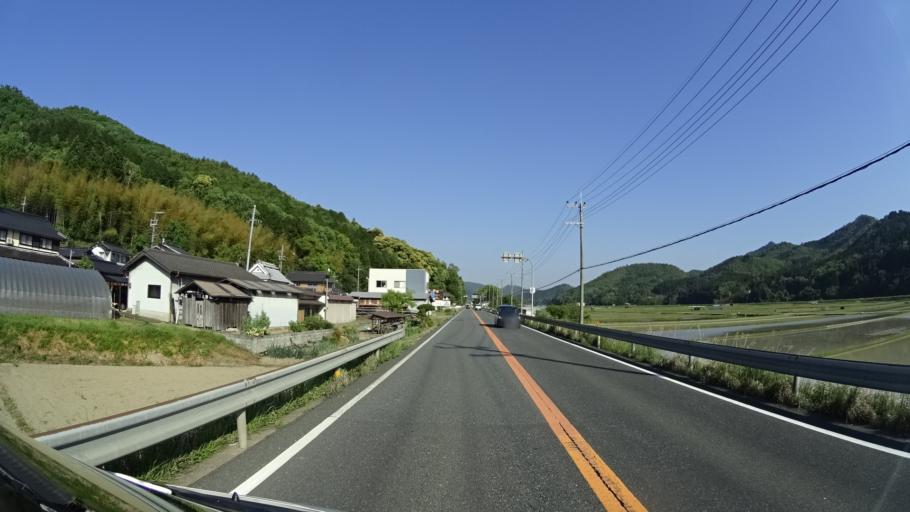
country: JP
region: Kyoto
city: Ayabe
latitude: 35.2629
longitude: 135.1883
